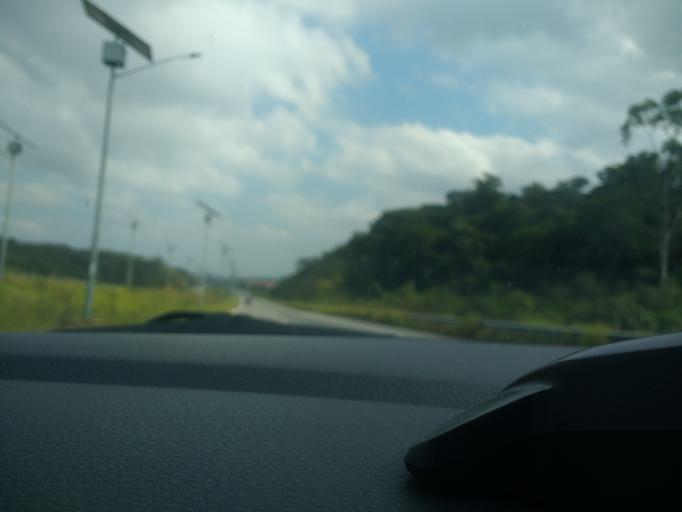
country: BR
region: Rio de Janeiro
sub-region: Queimados
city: Queimados
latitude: -22.6633
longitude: -43.5654
